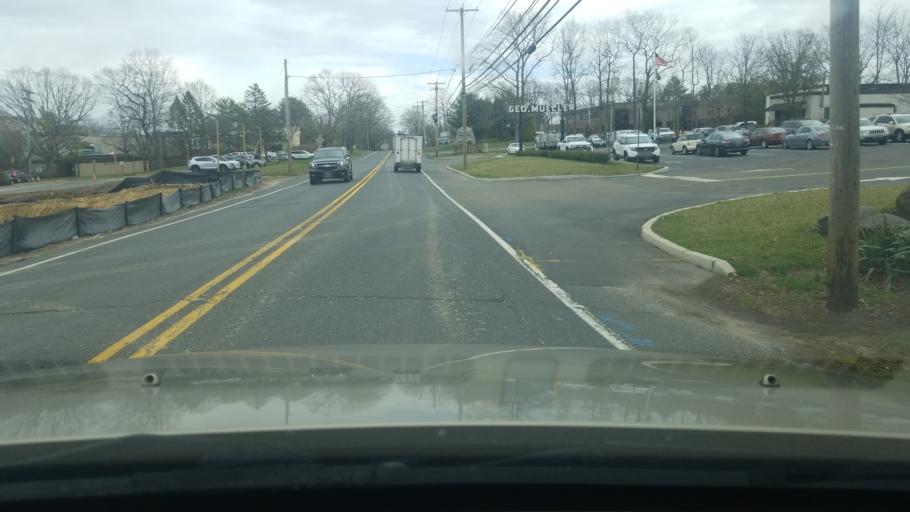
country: US
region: New Jersey
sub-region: Monmouth County
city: Manasquan
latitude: 40.1360
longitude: -74.0795
